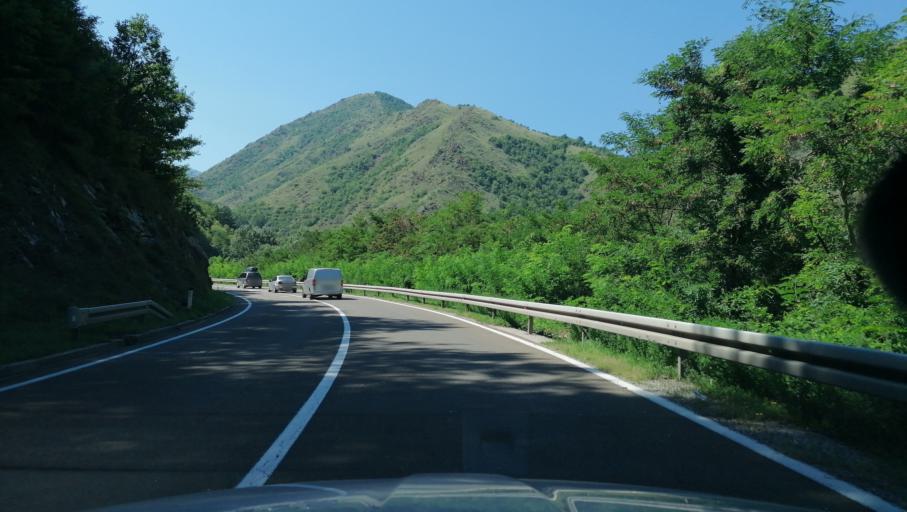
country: RS
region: Central Serbia
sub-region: Raski Okrug
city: Kraljevo
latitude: 43.5819
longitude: 20.5836
